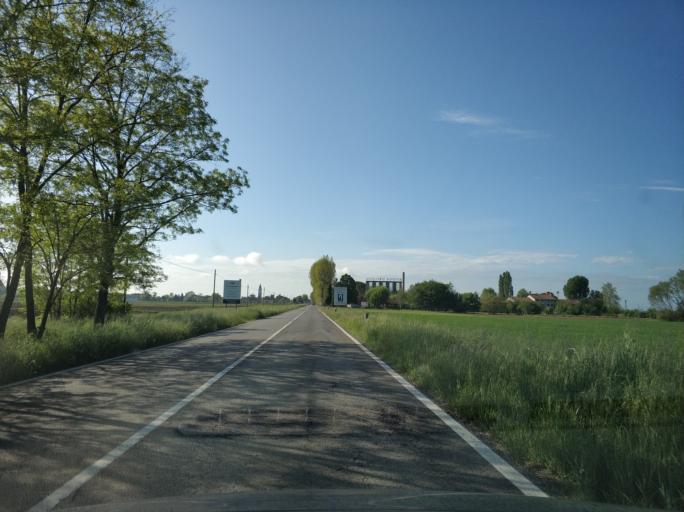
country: IT
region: Friuli Venezia Giulia
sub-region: Provincia di Udine
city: Aquileia
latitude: 45.7849
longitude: 13.3595
